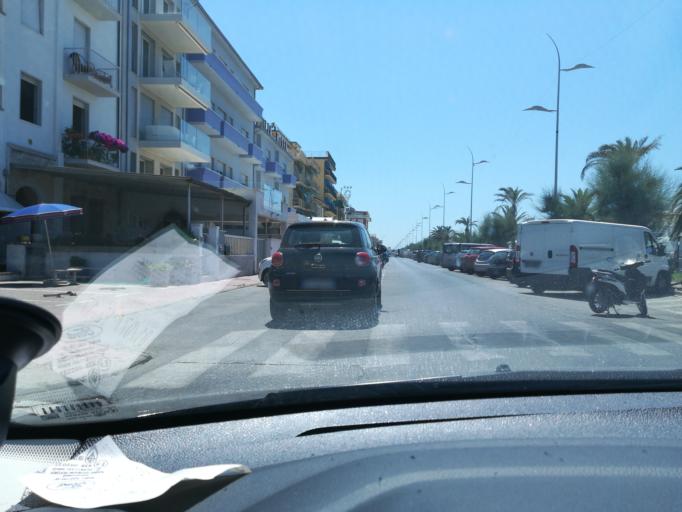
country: IT
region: Tuscany
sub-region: Provincia di Lucca
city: Camaiore
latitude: 43.8958
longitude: 10.2238
